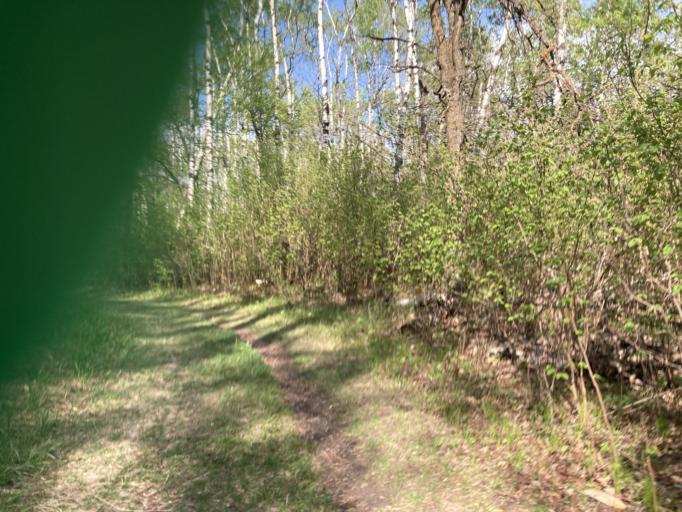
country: CA
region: Manitoba
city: Brandon
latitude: 49.7181
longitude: -99.9003
